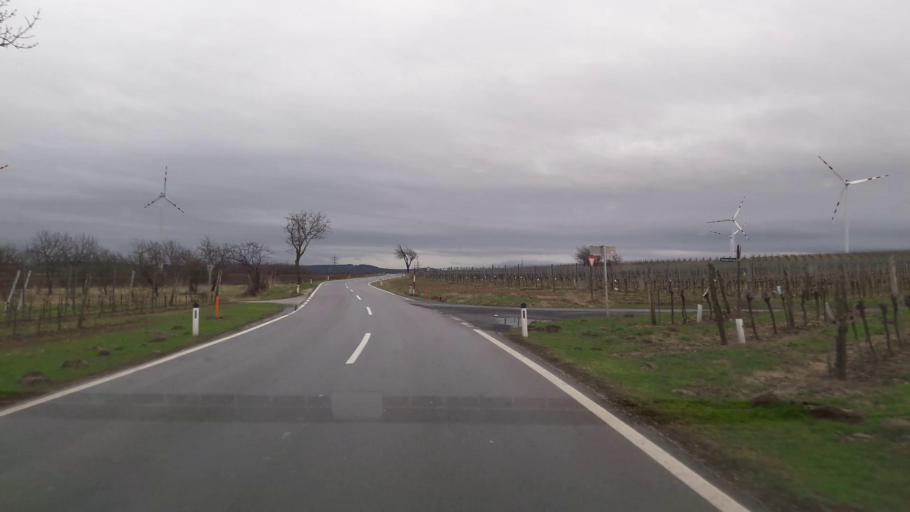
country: AT
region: Lower Austria
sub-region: Politischer Bezirk Bruck an der Leitha
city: Scharndorf
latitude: 48.0613
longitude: 16.7910
